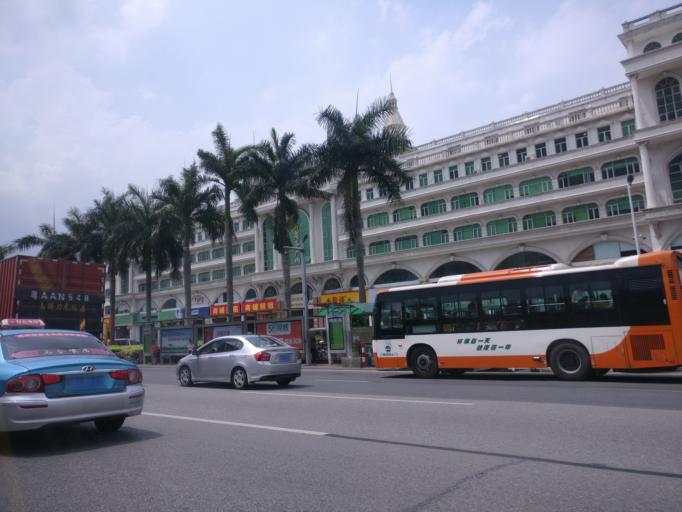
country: CN
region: Guangdong
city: Luopu
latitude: 23.0411
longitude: 113.3046
